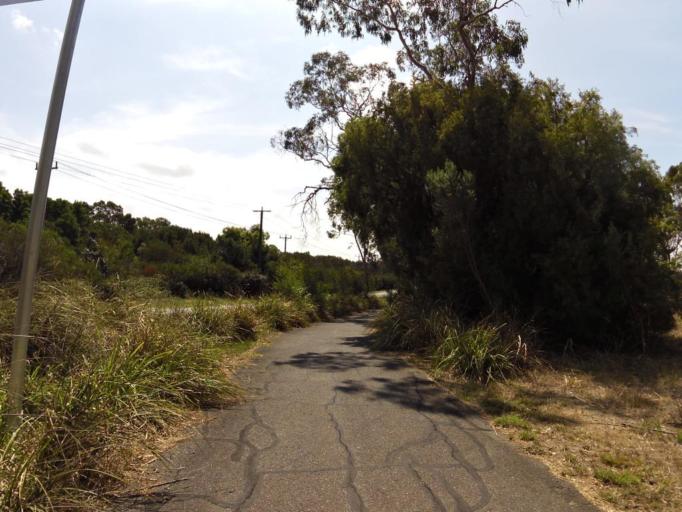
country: AU
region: Victoria
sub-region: Mornington Peninsula
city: Hastings
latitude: -38.3266
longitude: 145.1832
